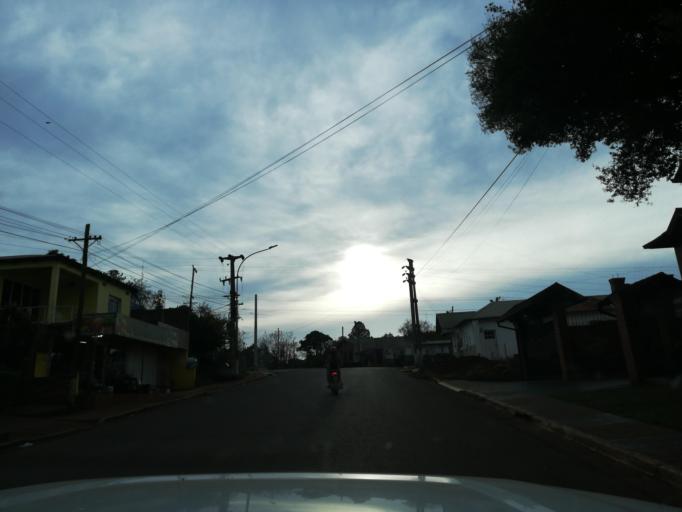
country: AR
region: Misiones
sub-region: Departamento de San Pedro
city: San Pedro
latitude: -26.6210
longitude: -54.1075
